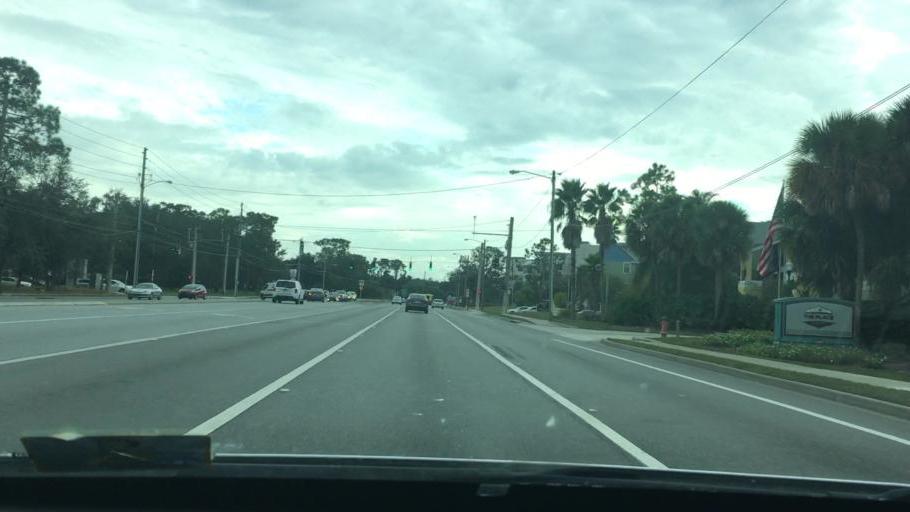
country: US
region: Florida
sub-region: Orange County
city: Alafaya
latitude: 28.5887
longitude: -81.2086
